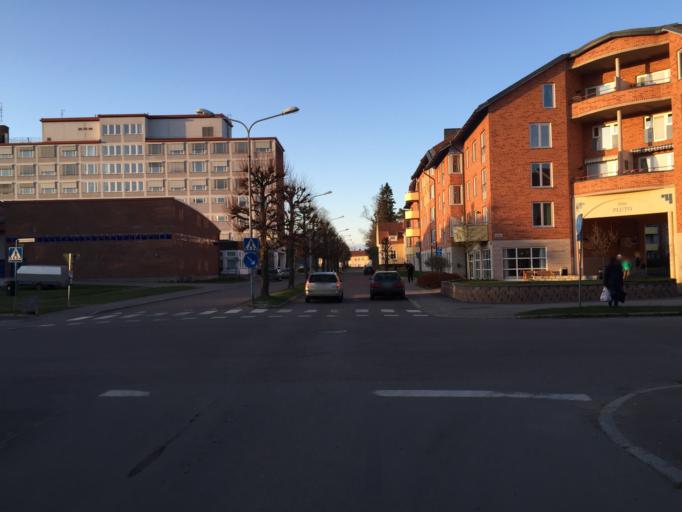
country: SE
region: Dalarna
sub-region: Ludvika Kommun
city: Ludvika
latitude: 60.1478
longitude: 15.1892
